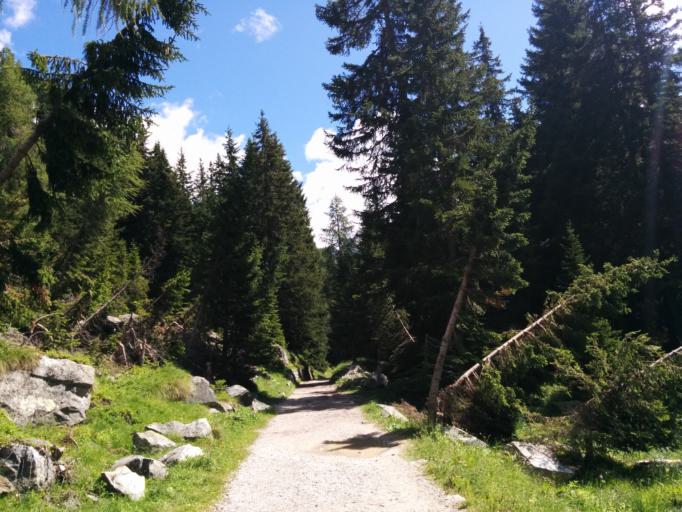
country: IT
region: Lombardy
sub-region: Provincia di Brescia
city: Saviore
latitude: 46.0708
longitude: 10.5340
